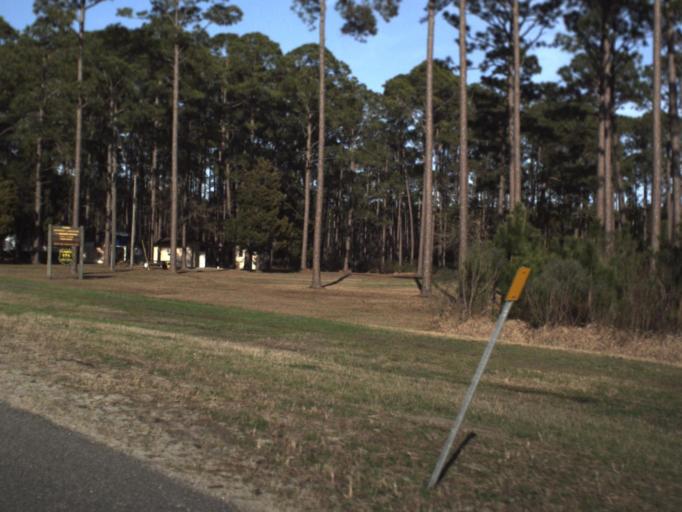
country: US
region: Florida
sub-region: Bay County
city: Laguna Beach
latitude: 30.3000
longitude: -85.8526
